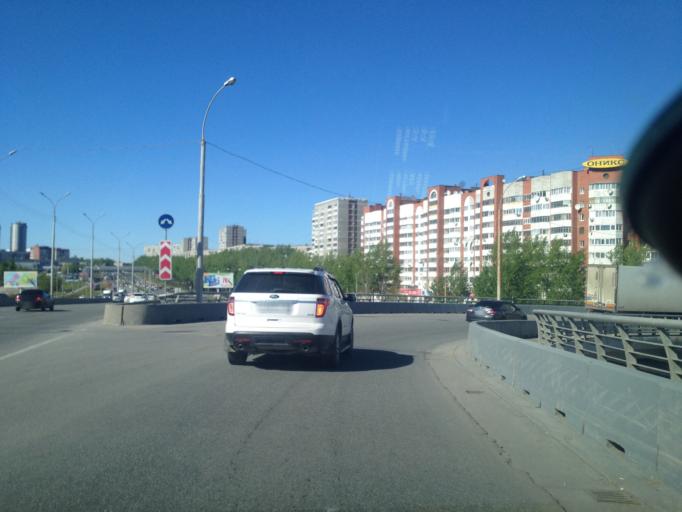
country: RU
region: Sverdlovsk
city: Yekaterinburg
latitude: 56.8603
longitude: 60.5500
